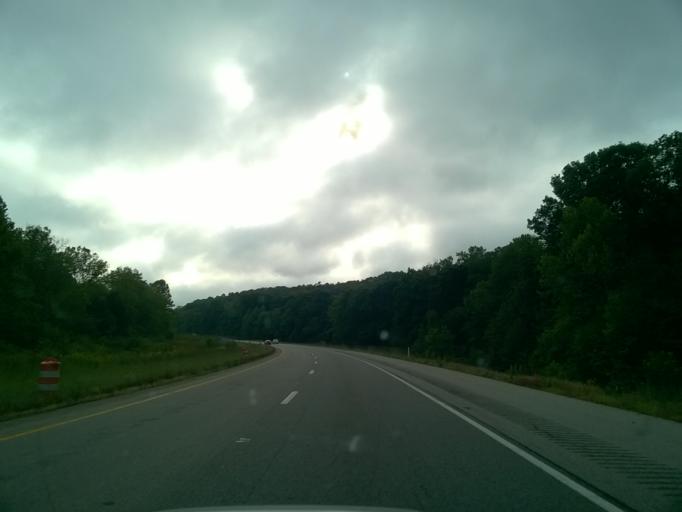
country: US
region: Indiana
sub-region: Crawford County
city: English
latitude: 38.2376
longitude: -86.4001
